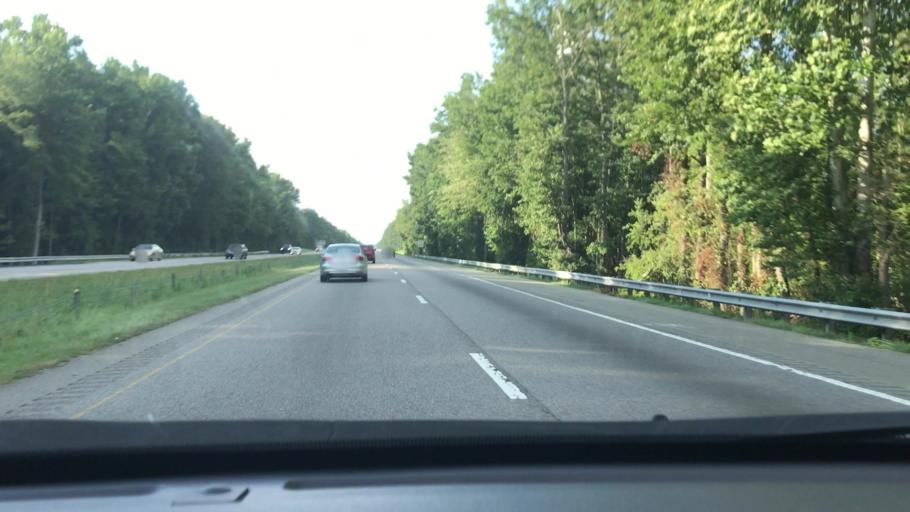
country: US
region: North Carolina
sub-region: Robeson County
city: Saint Pauls
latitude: 34.7277
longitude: -78.9972
